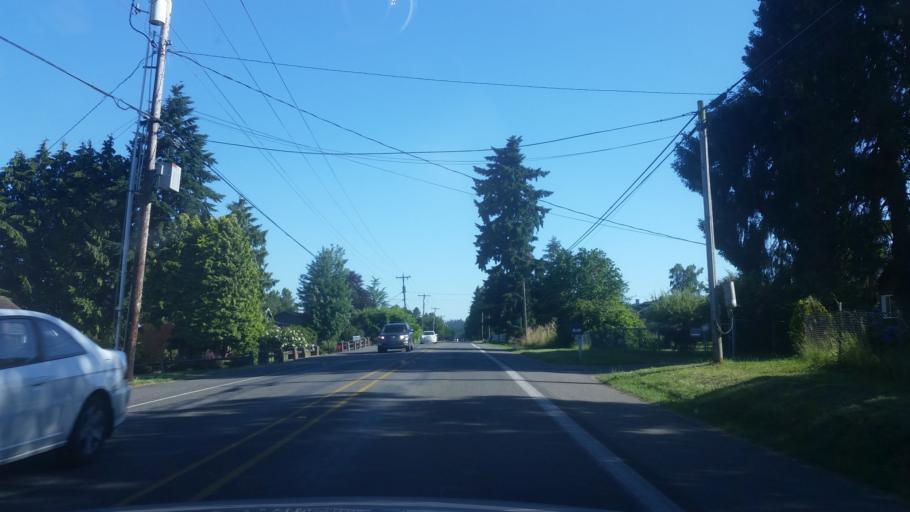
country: US
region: Washington
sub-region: Snohomish County
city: Cathcart
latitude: 47.8615
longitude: -122.0991
